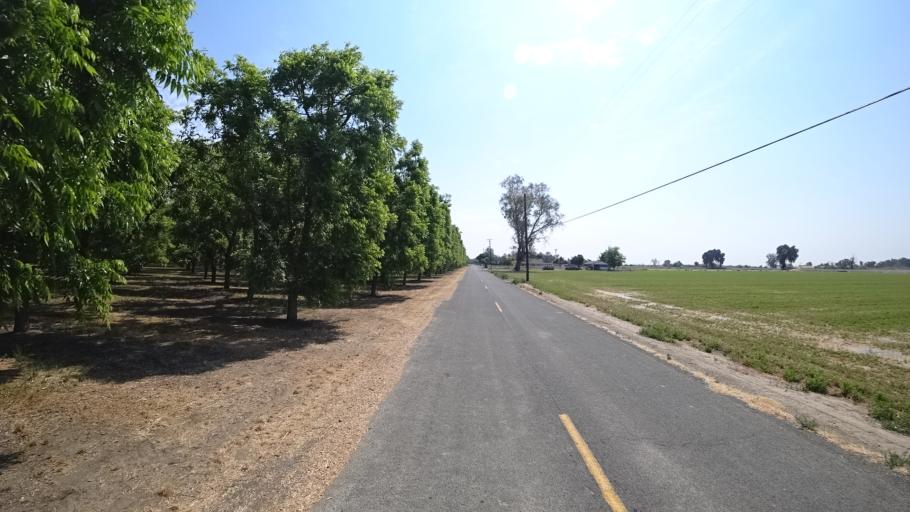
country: US
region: California
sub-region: Fresno County
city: Laton
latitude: 36.3948
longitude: -119.7706
